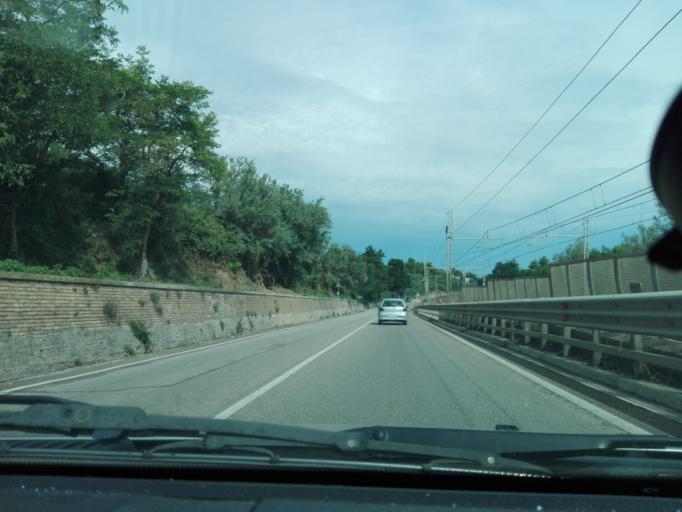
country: IT
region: Abruzzo
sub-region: Provincia di Teramo
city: Pineto
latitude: 42.5852
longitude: 14.0887
